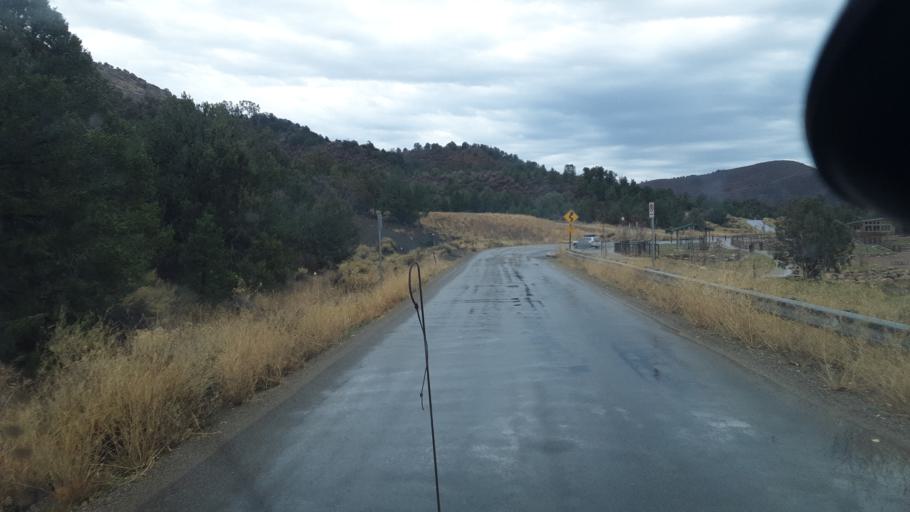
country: US
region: Colorado
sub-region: La Plata County
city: Durango
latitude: 37.2343
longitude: -107.9067
